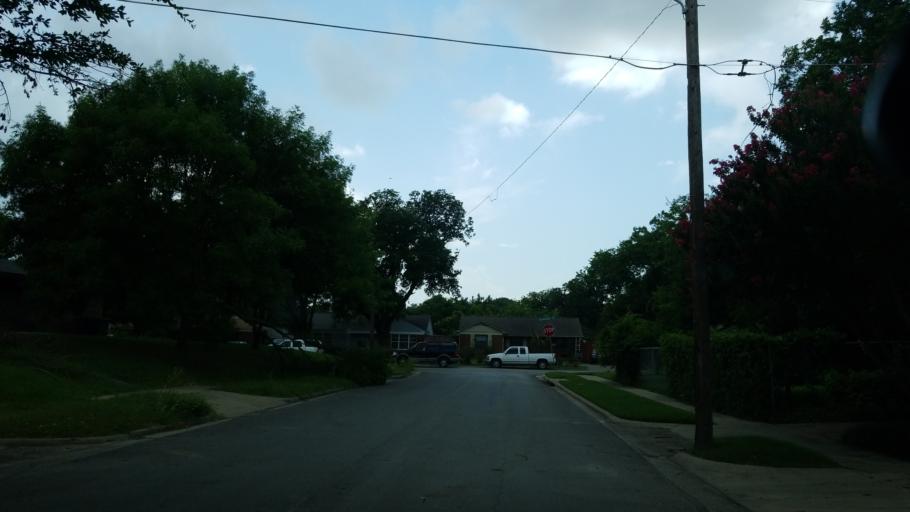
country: US
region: Texas
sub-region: Dallas County
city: Farmers Branch
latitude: 32.8779
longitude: -96.8622
